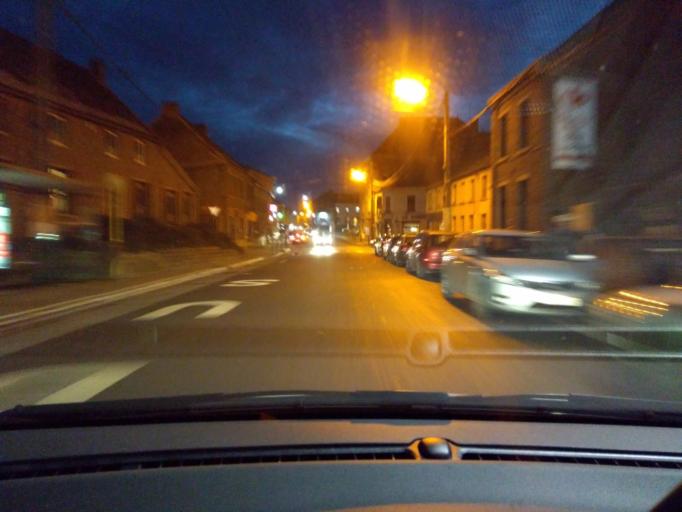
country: BE
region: Wallonia
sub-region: Province du Hainaut
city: Roeulx
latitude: 50.4644
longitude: 4.0468
